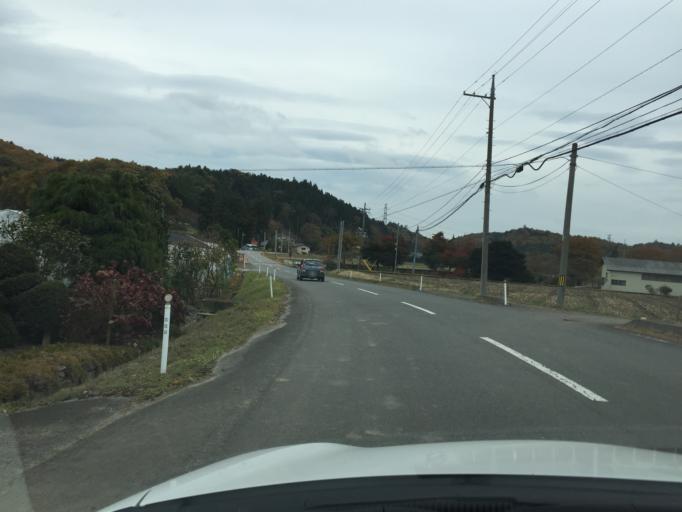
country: JP
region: Fukushima
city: Iwaki
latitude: 37.1802
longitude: 140.7190
